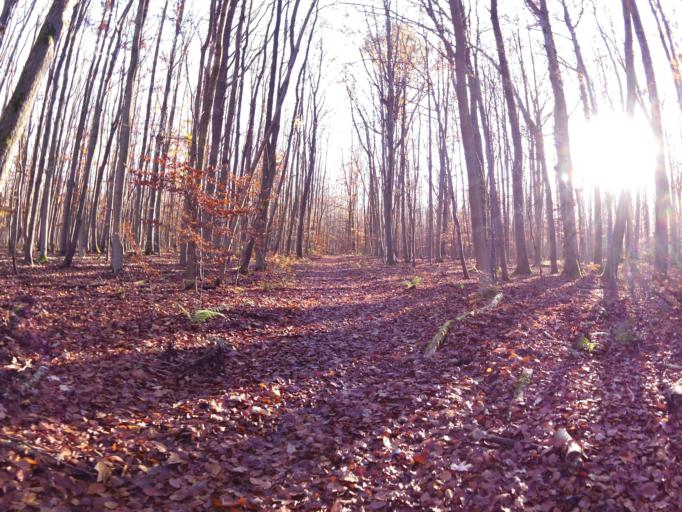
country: DE
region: Thuringia
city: Kammerforst
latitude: 51.0620
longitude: 10.4447
